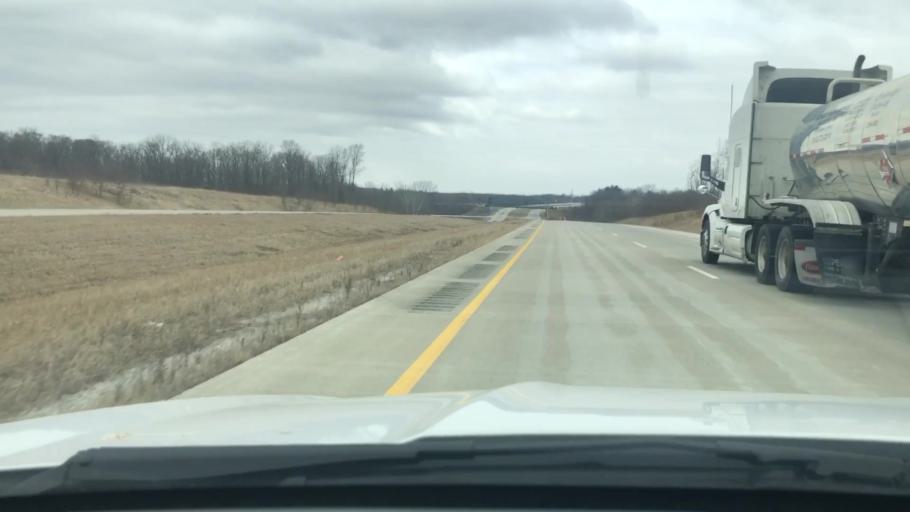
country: US
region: Indiana
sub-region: Carroll County
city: Delphi
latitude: 40.5864
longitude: -86.6508
